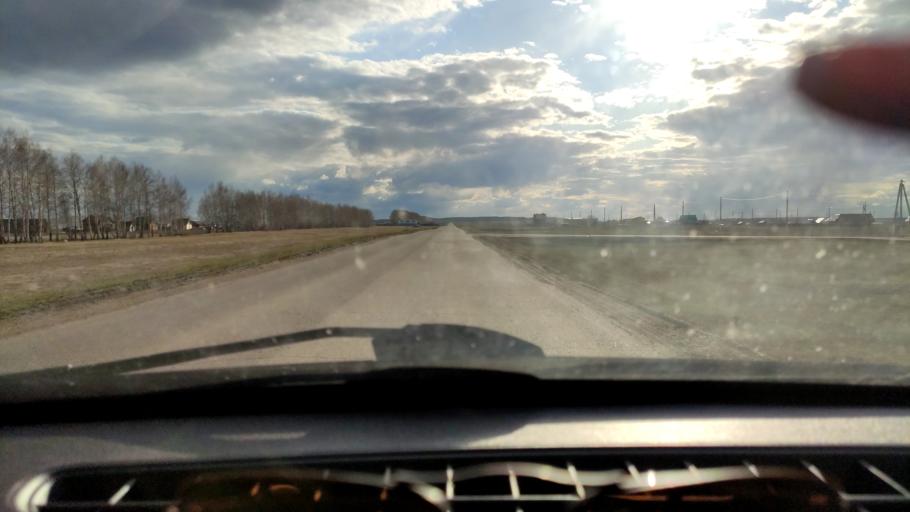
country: RU
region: Bashkortostan
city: Karmaskaly
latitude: 54.3541
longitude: 56.1416
